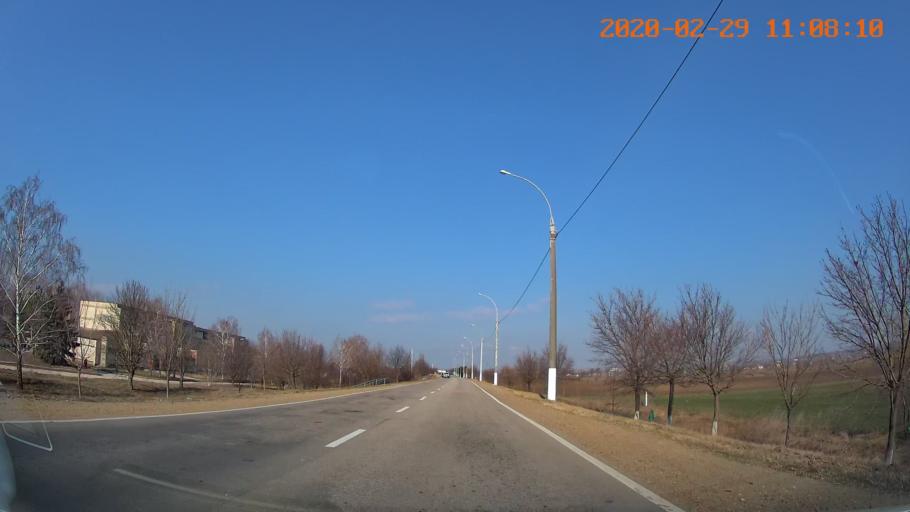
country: MD
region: Criuleni
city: Criuleni
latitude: 47.2316
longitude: 29.1774
